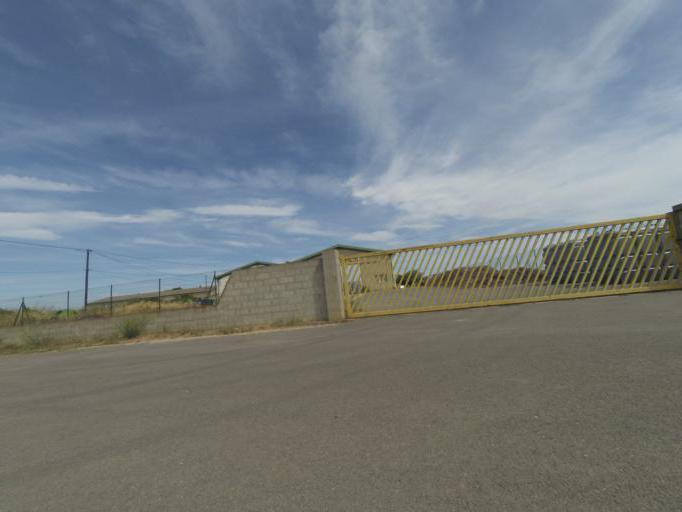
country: FR
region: Languedoc-Roussillon
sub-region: Departement du Gard
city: Aimargues
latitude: 43.6998
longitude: 4.2043
